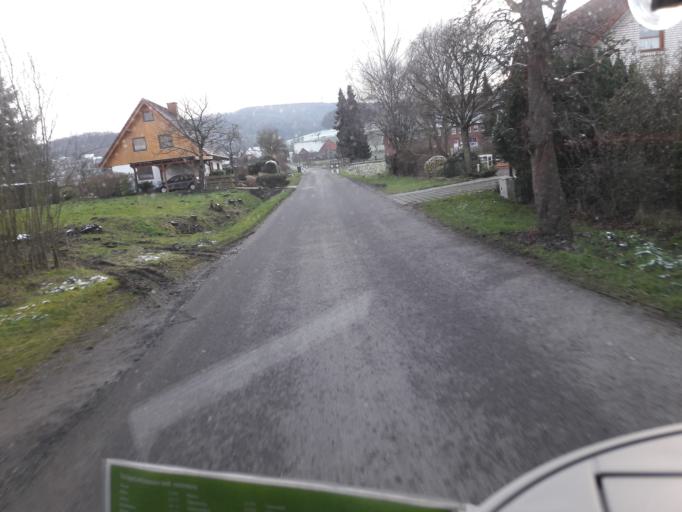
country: DE
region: Lower Saxony
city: Buckeburg
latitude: 52.2356
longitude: 9.0598
